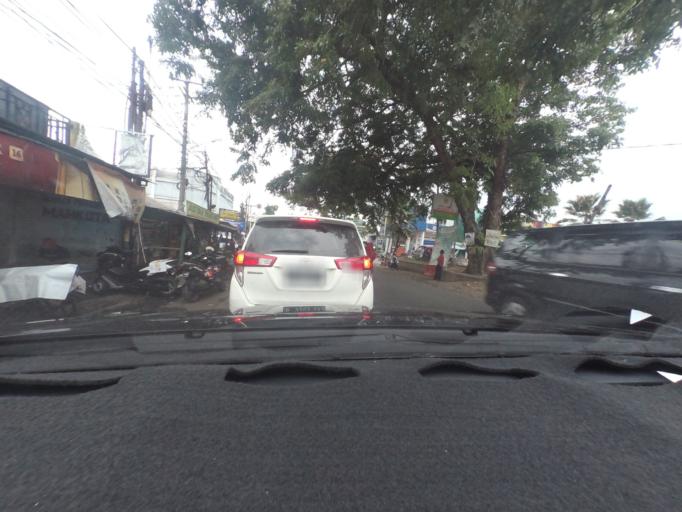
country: ID
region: West Java
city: Cicurug
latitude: -6.7972
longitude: 106.7774
